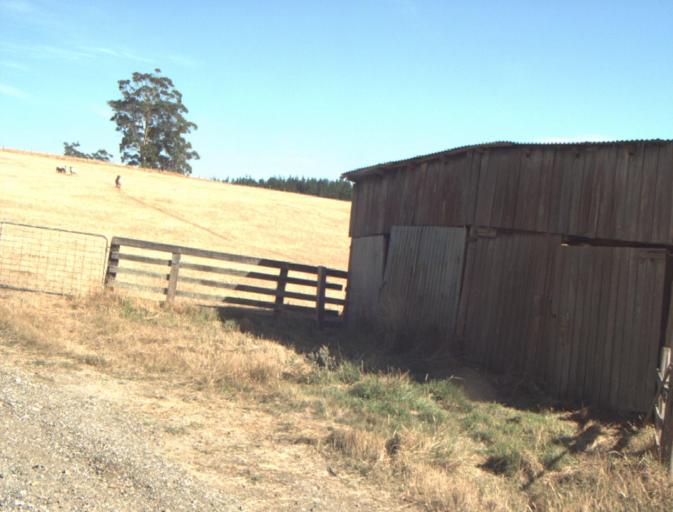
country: AU
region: Tasmania
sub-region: Launceston
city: Mayfield
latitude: -41.1715
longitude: 147.2066
